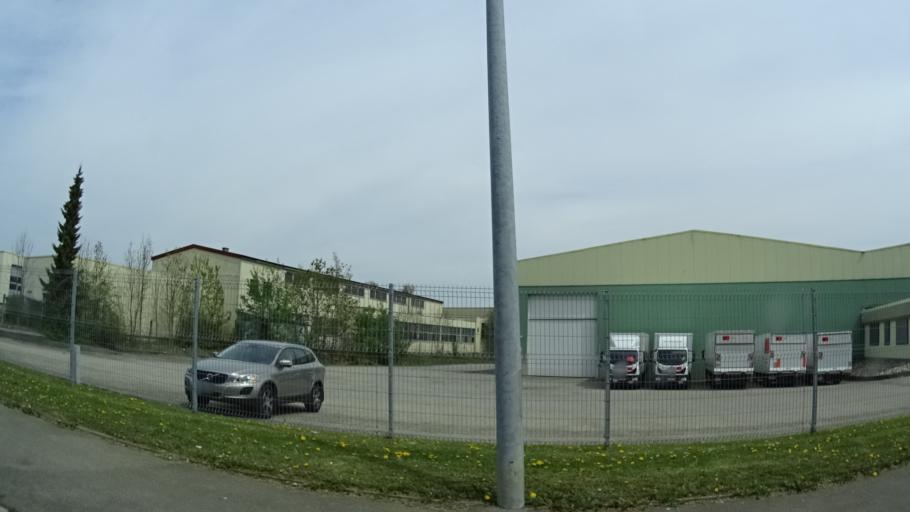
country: DE
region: Baden-Wuerttemberg
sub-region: Freiburg Region
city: Dauchingen
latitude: 48.0608
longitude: 8.5551
